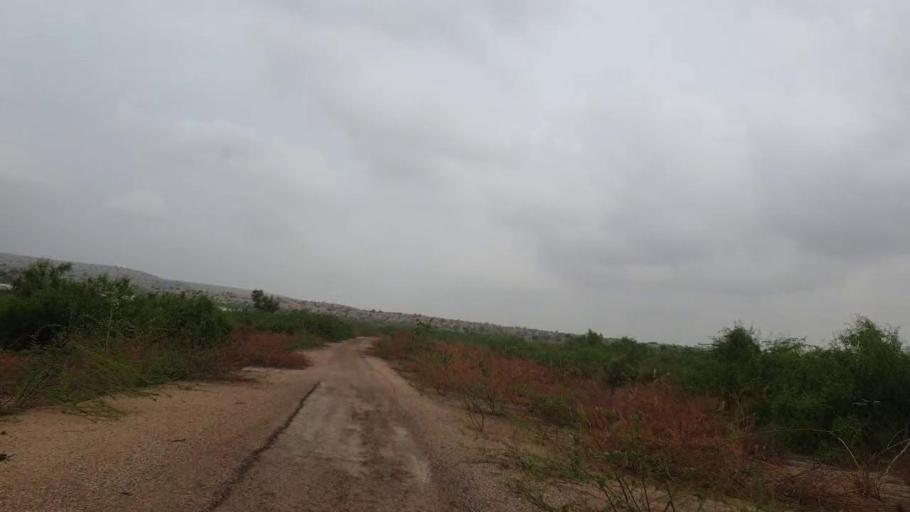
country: PK
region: Sindh
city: Diplo
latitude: 24.5213
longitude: 69.4690
